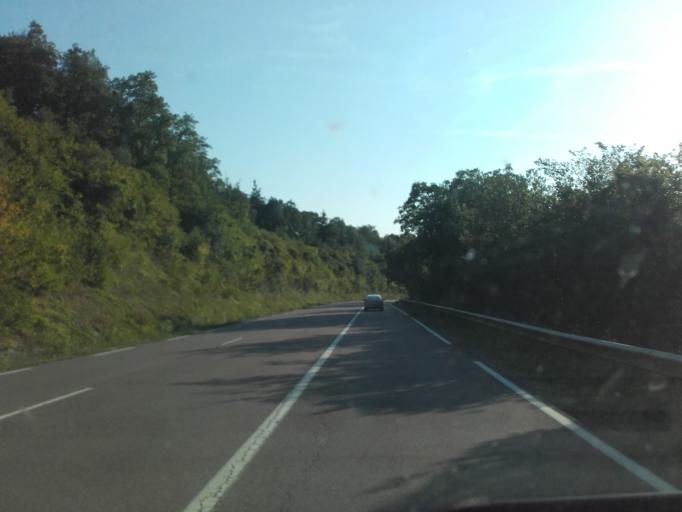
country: FR
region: Bourgogne
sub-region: Departement de l'Yonne
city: Venoy
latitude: 47.8083
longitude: 3.6764
